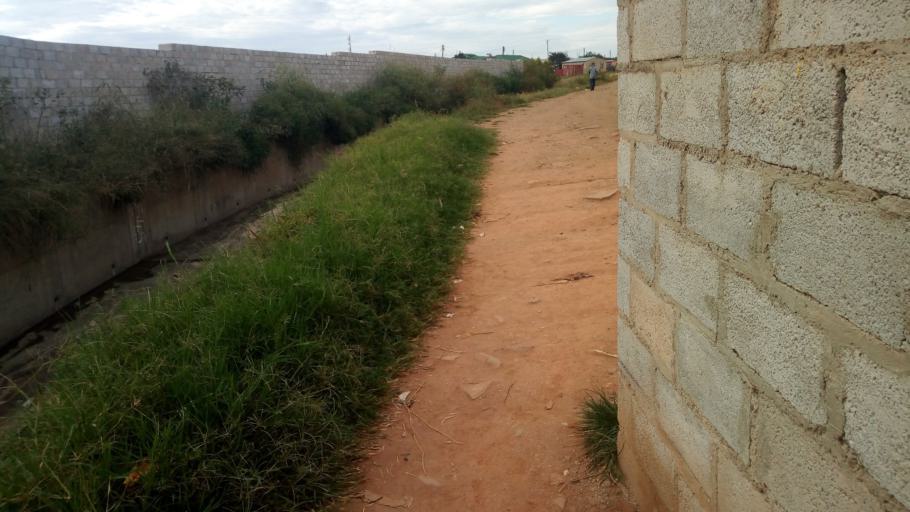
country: ZM
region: Lusaka
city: Lusaka
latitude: -15.3941
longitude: 28.2862
